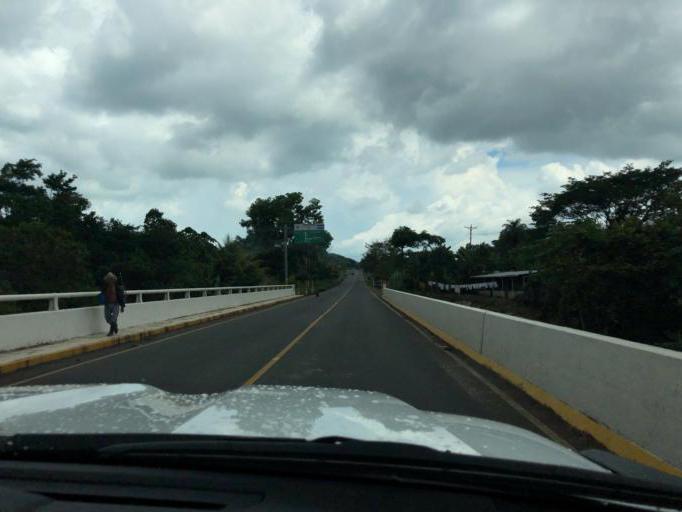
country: NI
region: Chontales
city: Villa Sandino
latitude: 11.9961
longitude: -84.8740
